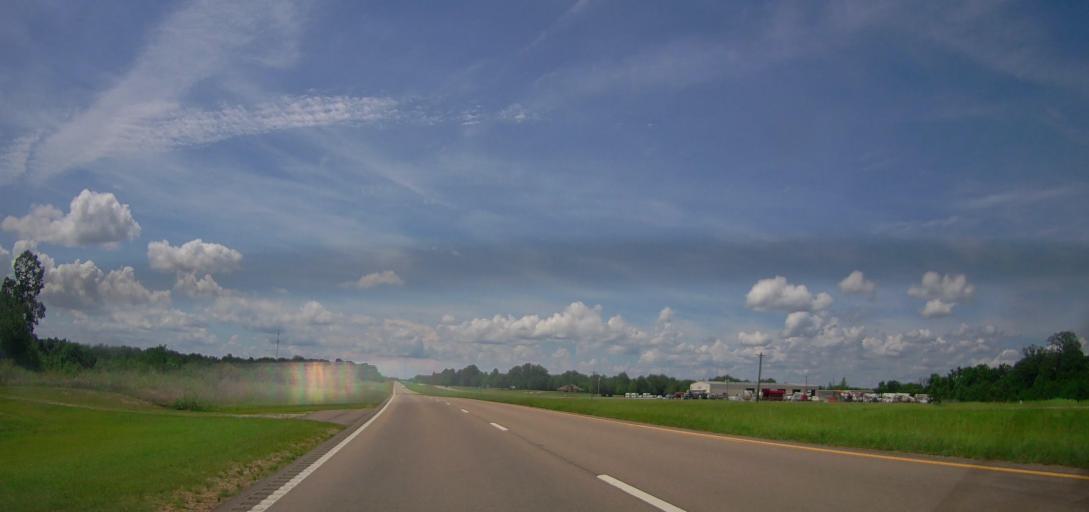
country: US
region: Mississippi
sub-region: Lee County
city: Nettleton
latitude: 33.9779
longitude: -88.6149
